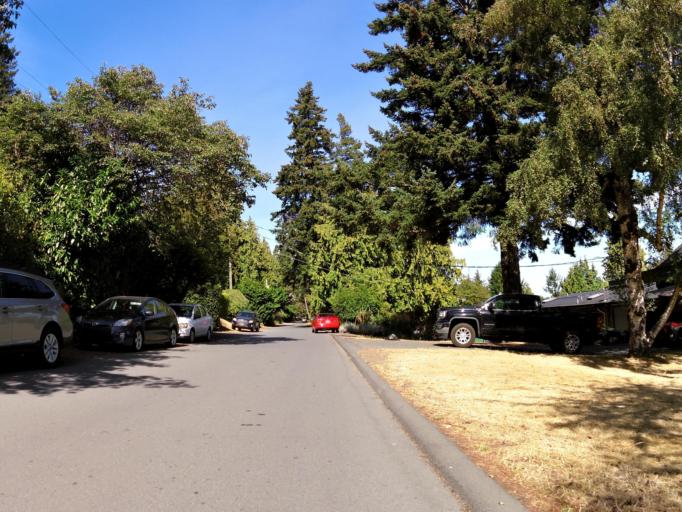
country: CA
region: British Columbia
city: Victoria
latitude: 48.5147
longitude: -123.3674
